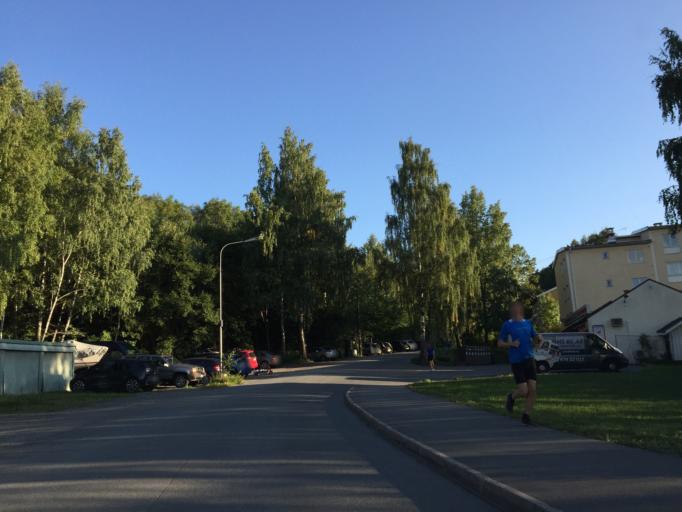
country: NO
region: Akershus
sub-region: Baerum
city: Lysaker
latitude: 59.9036
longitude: 10.6150
